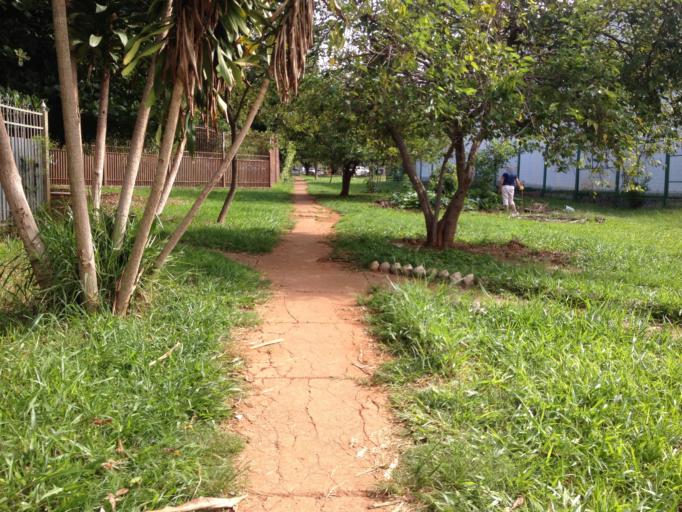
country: BR
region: Federal District
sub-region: Brasilia
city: Brasilia
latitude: -15.8419
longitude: -47.9781
